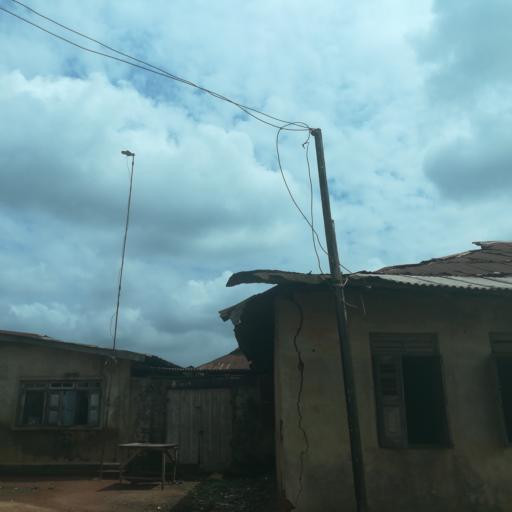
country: NG
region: Lagos
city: Ejirin
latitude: 6.6429
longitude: 3.7124
